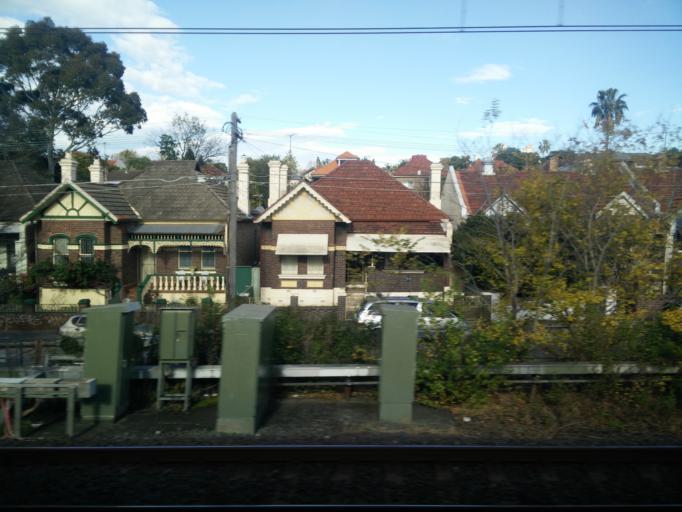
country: AU
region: New South Wales
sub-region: Marrickville
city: Camperdown
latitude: -33.8947
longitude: 151.1695
